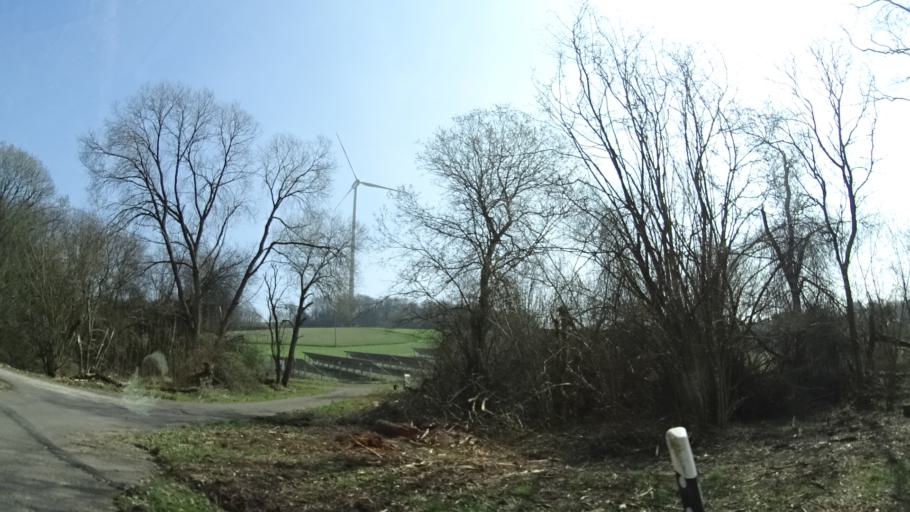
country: DE
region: Rheinland-Pfalz
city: Gimbweiler
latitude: 49.5919
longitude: 7.1984
